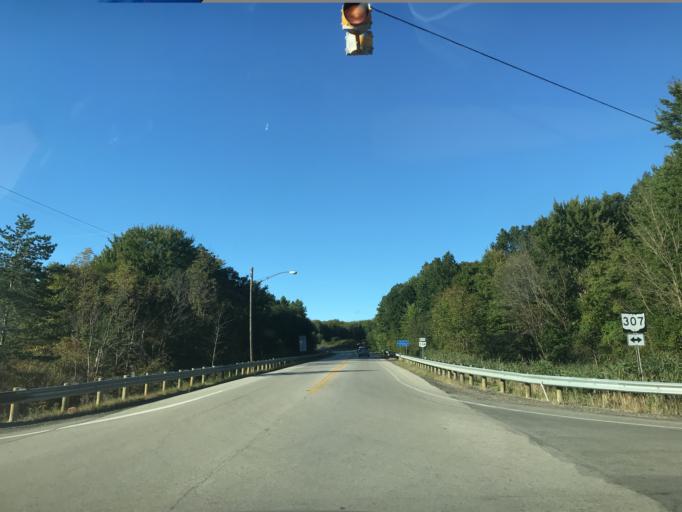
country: US
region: Ohio
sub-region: Ashtabula County
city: Geneva
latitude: 41.7597
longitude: -80.9412
